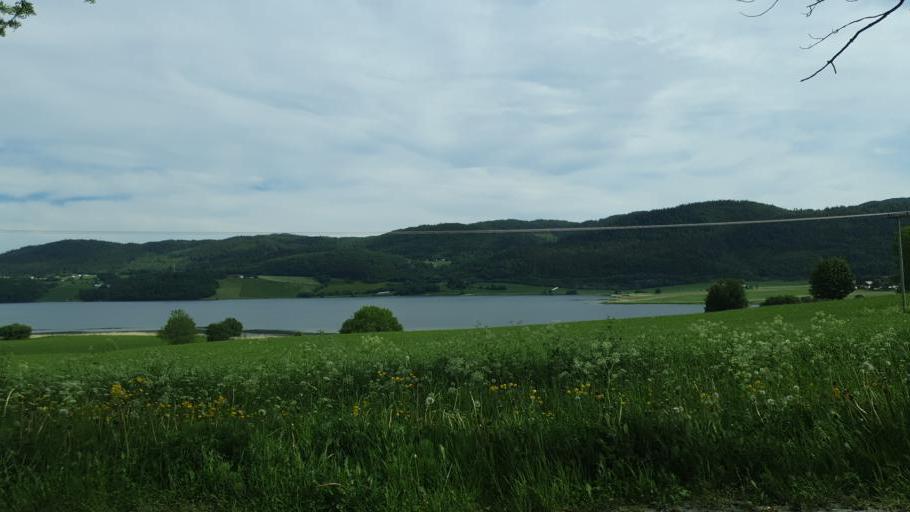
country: NO
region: Sor-Trondelag
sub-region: Rissa
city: Rissa
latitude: 63.5663
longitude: 9.9279
